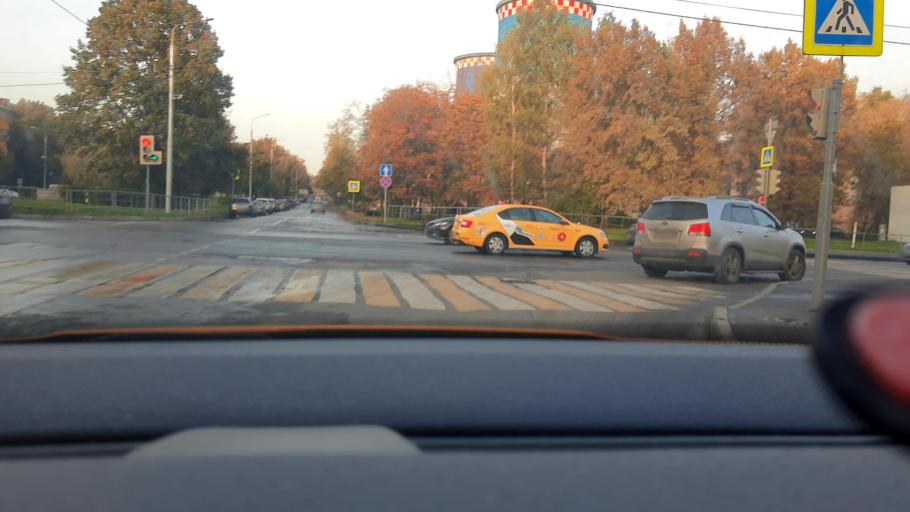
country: RU
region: Moscow
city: Metrogorodok
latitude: 55.8214
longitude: 37.7622
